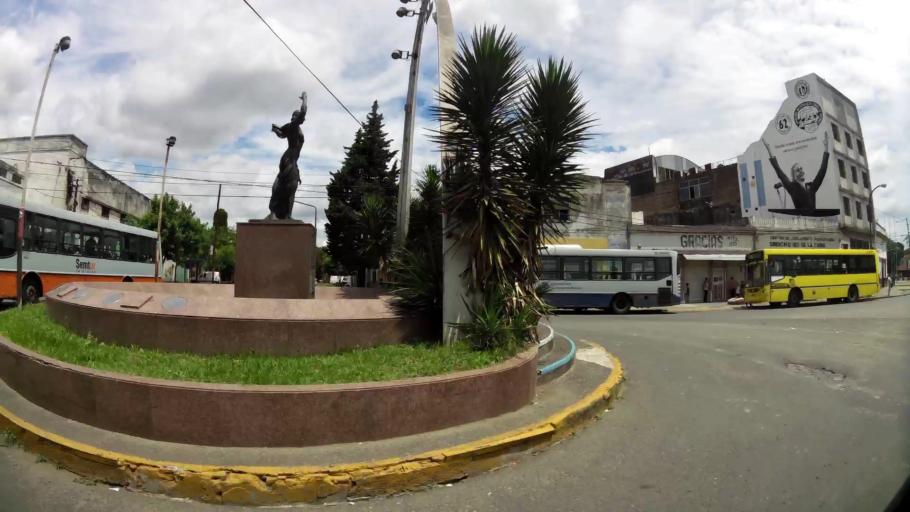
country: AR
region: Santa Fe
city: Gobernador Galvez
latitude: -32.9980
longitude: -60.6203
